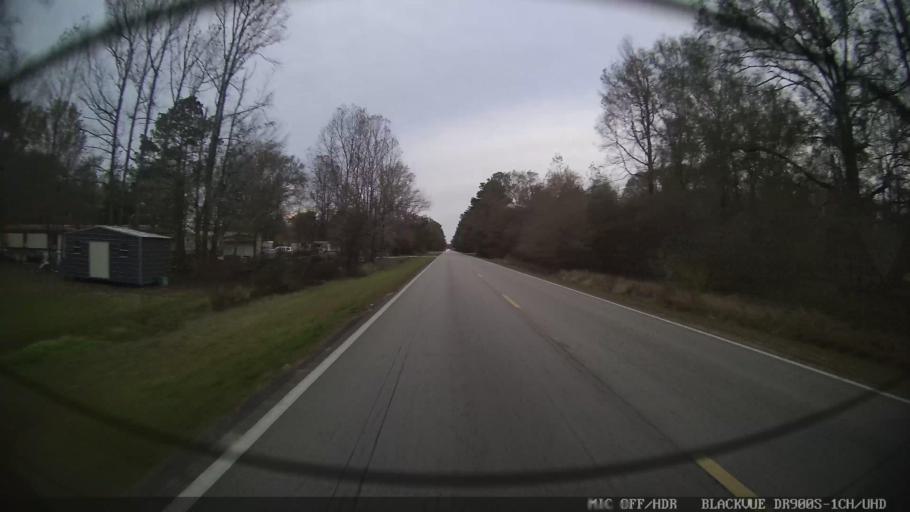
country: US
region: Mississippi
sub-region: Clarke County
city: Stonewall
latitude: 32.0291
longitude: -88.8642
